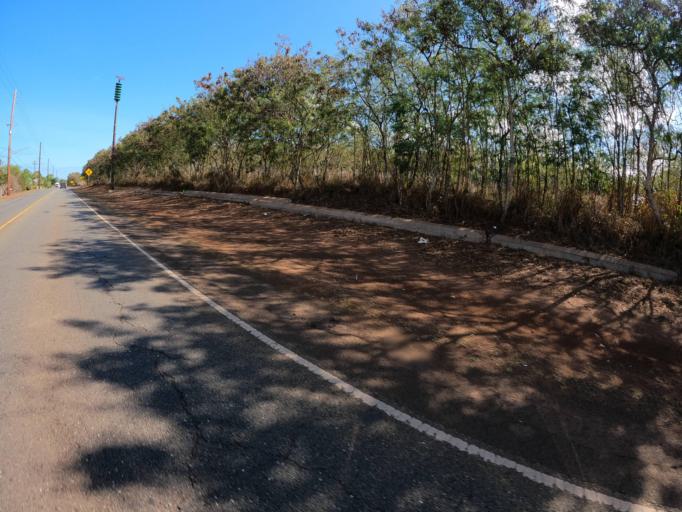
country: US
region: Hawaii
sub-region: Honolulu County
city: Hale'iwa
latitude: 21.5713
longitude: -158.1082
